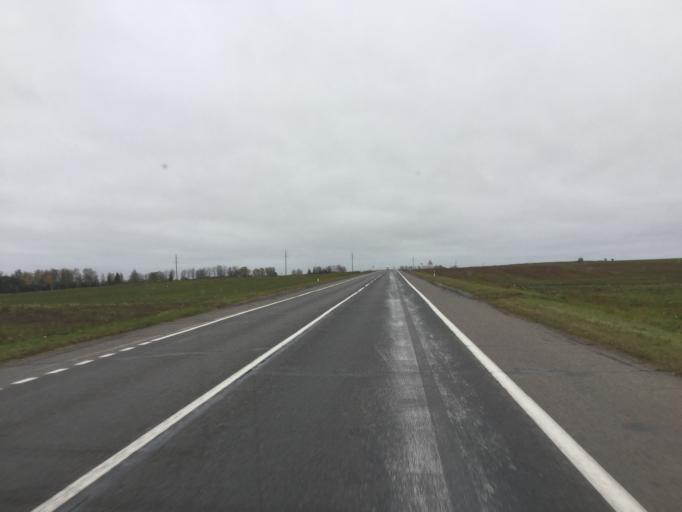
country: BY
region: Vitebsk
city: Chashniki
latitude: 55.0091
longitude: 29.1581
